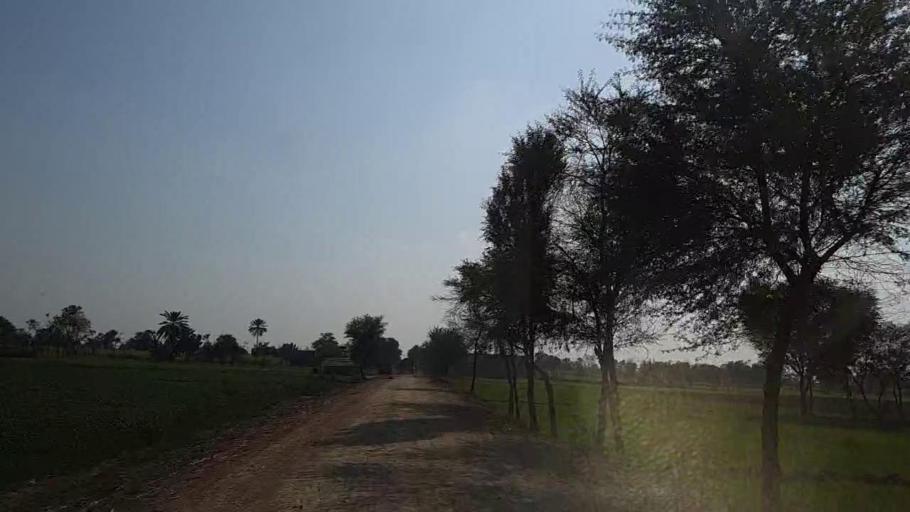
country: PK
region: Sindh
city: Daur
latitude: 26.4290
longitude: 68.2369
